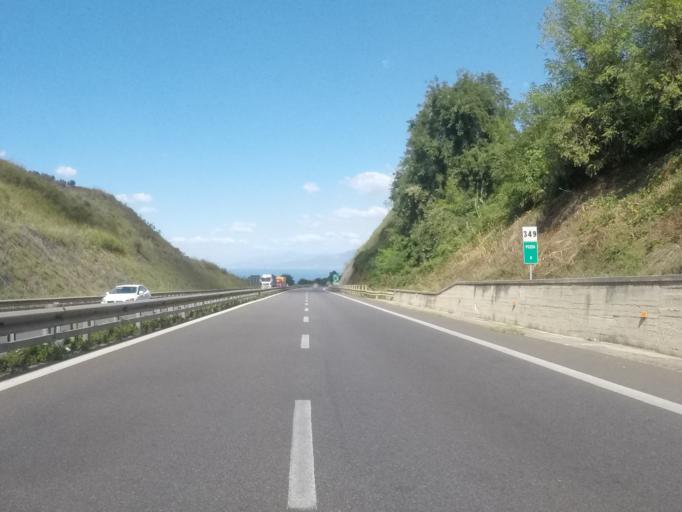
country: IT
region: Calabria
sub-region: Provincia di Vibo-Valentia
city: Sant'Onofrio
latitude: 38.7105
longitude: 16.1539
